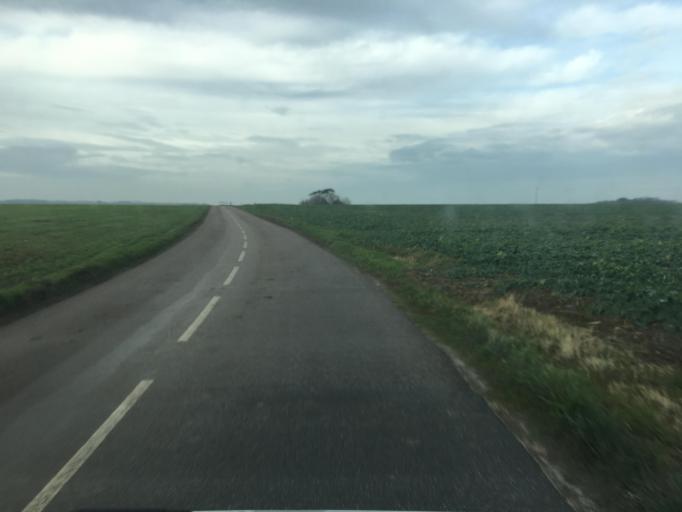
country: FR
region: Lower Normandy
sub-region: Departement du Calvados
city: Ver-sur-Mer
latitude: 49.3204
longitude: -0.5541
